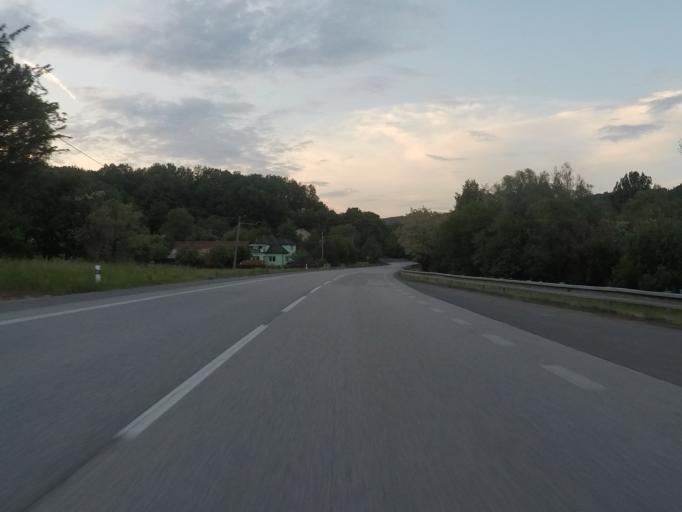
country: SK
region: Banskobystricky
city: Rimavska Sobota
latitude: 48.4721
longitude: 19.9498
